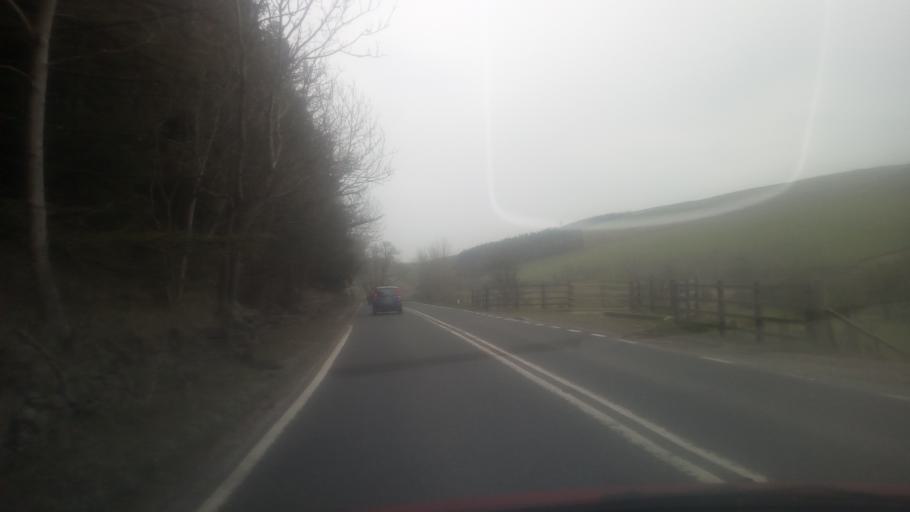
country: GB
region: Scotland
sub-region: The Scottish Borders
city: Galashiels
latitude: 55.7030
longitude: -2.8894
